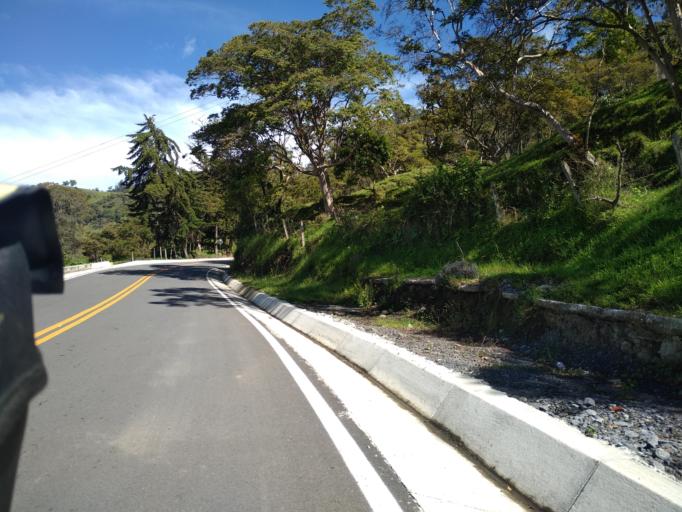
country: CO
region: Santander
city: Velez
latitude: 6.0004
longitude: -73.6919
